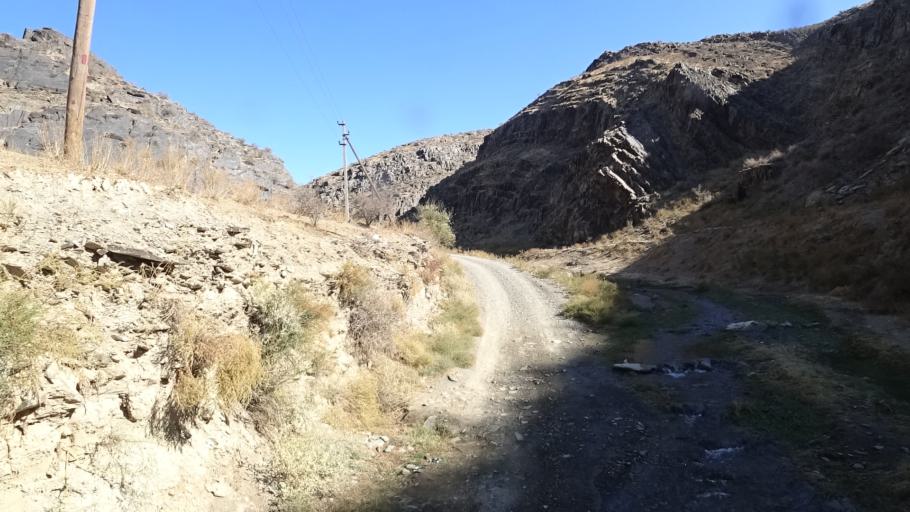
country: UZ
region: Navoiy
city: Nurota
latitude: 40.3062
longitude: 65.6182
